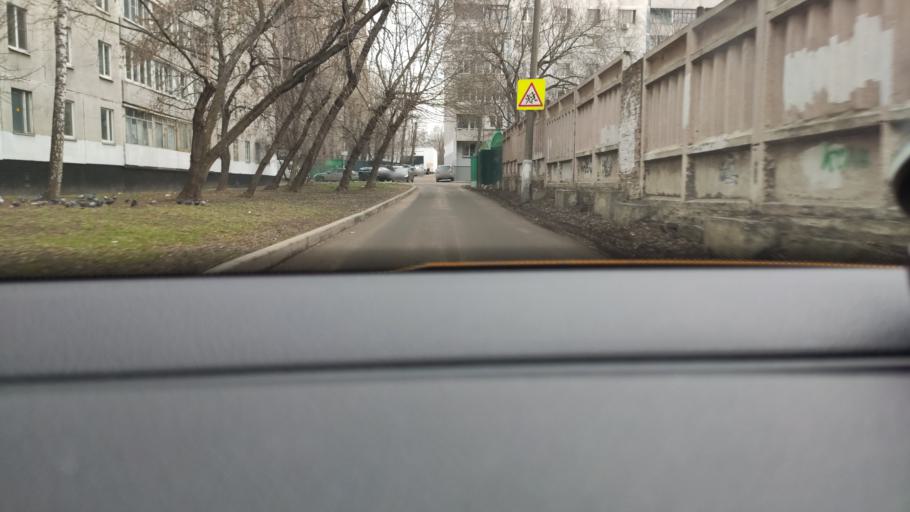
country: RU
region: Moscow
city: Slobodka
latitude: 55.8746
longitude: 37.5758
